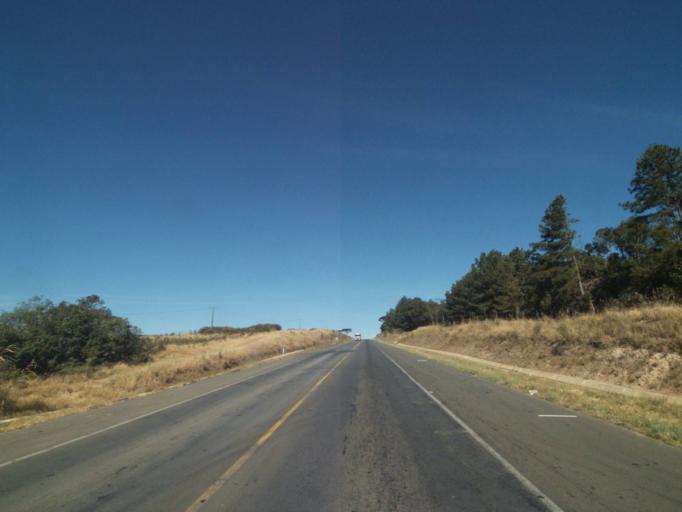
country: BR
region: Parana
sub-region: Tibagi
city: Tibagi
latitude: -24.7951
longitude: -50.4665
